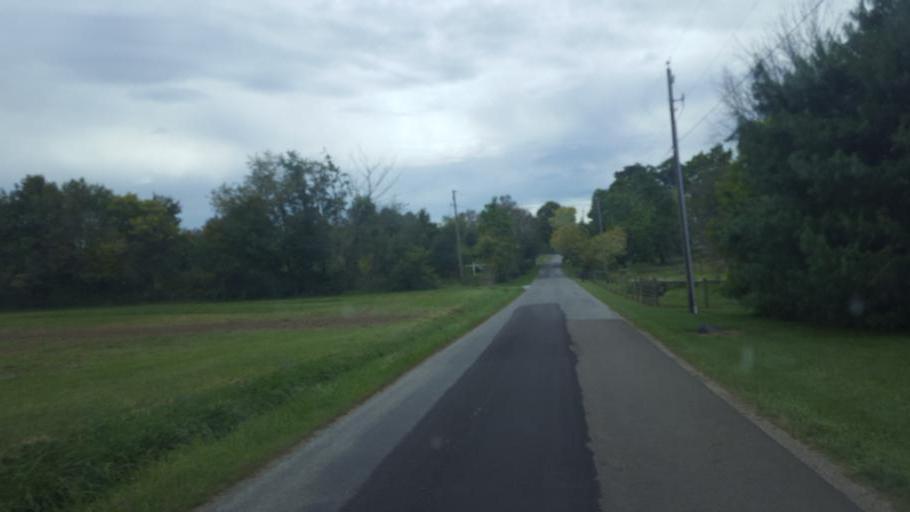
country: US
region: Ohio
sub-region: Knox County
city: Centerburg
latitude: 40.3182
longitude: -82.7179
